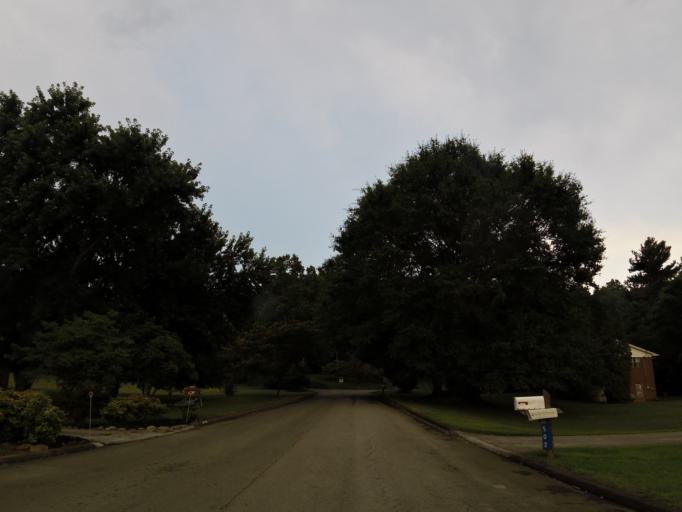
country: US
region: Tennessee
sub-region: Blount County
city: Eagleton Village
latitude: 35.7957
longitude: -83.9327
